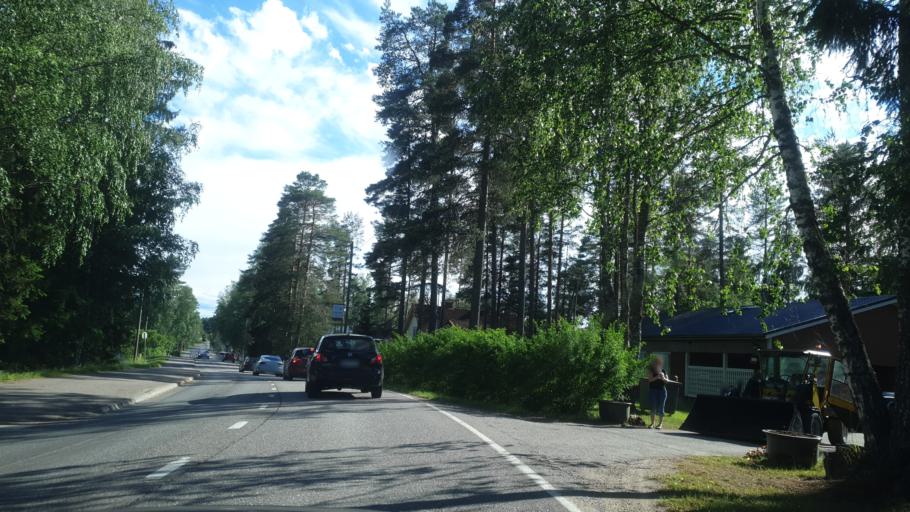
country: FI
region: Southern Savonia
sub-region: Mikkeli
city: Pertunmaa
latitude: 61.5088
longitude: 26.4830
